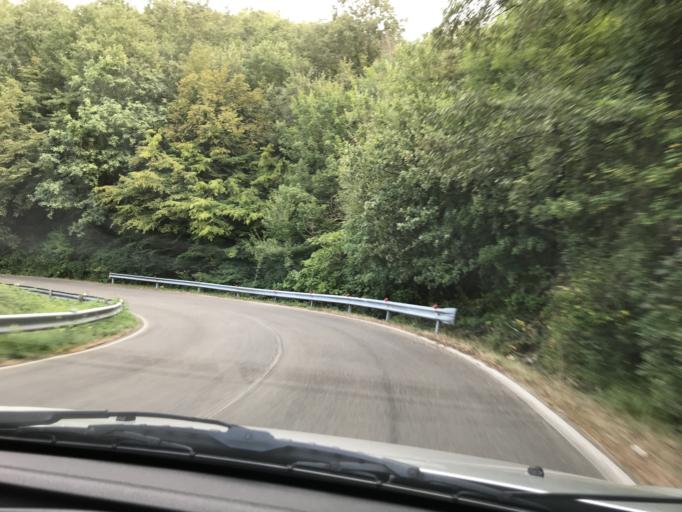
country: IT
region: Umbria
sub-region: Provincia di Terni
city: Guardea
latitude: 42.6530
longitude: 12.3498
